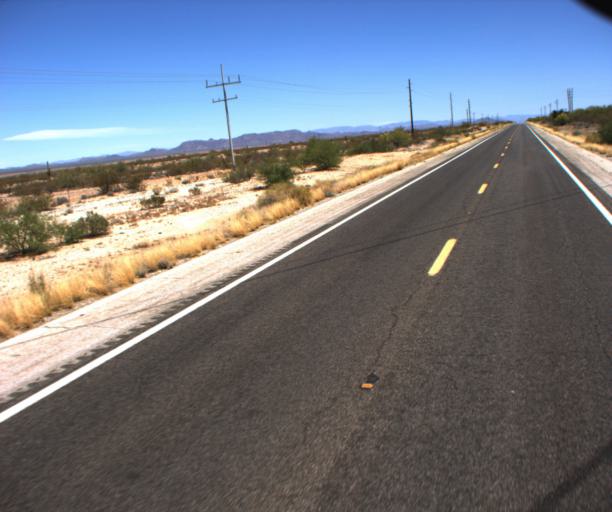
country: US
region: Arizona
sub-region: La Paz County
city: Salome
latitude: 33.9059
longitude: -113.2899
